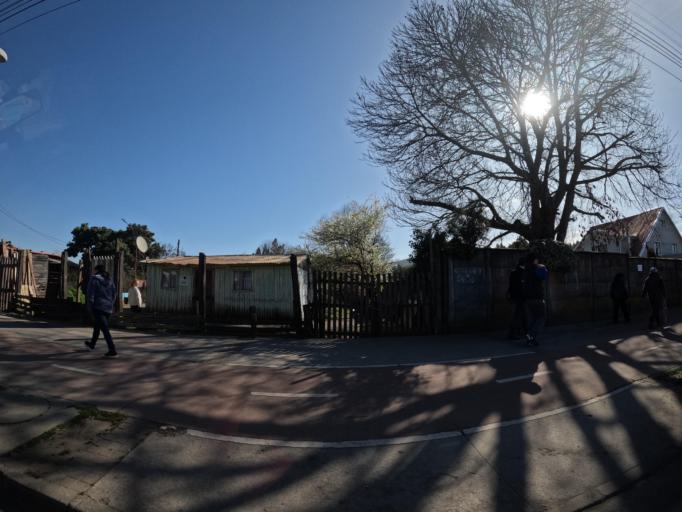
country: CL
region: Biobio
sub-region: Provincia de Concepcion
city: Chiguayante
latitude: -36.9700
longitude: -72.9364
